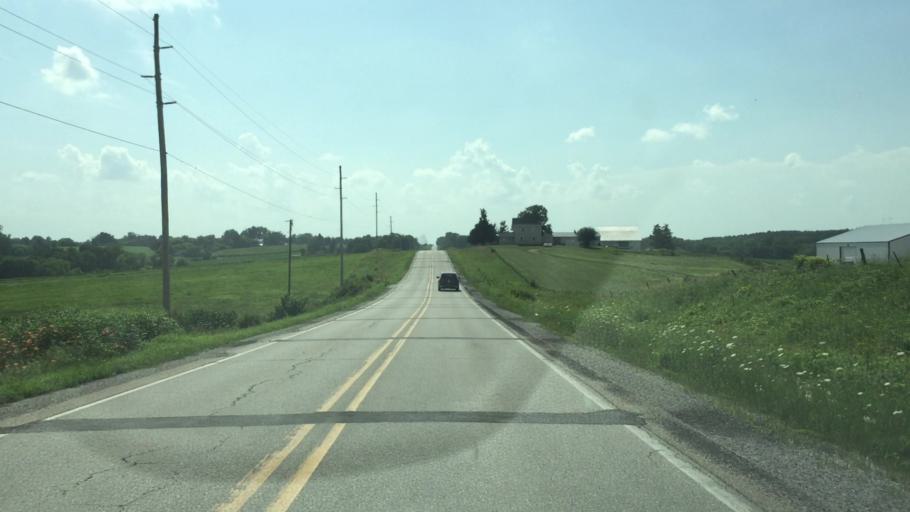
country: US
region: Iowa
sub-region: Linn County
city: Ely
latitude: 41.8475
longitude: -91.5880
